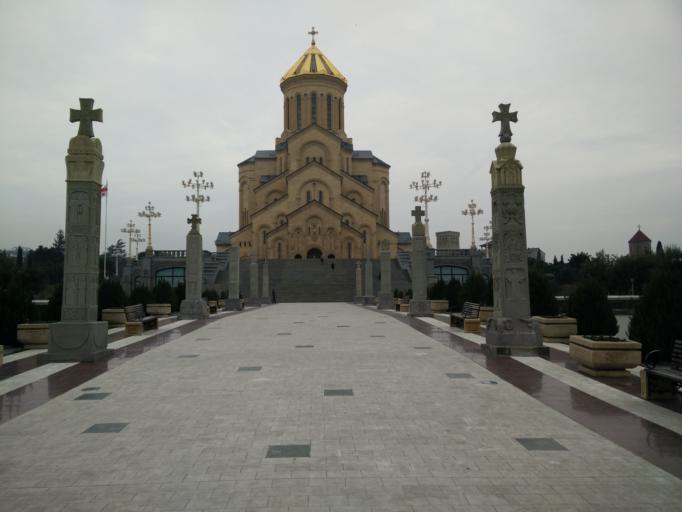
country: GE
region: T'bilisi
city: Tbilisi
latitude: 41.6975
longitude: 44.8146
